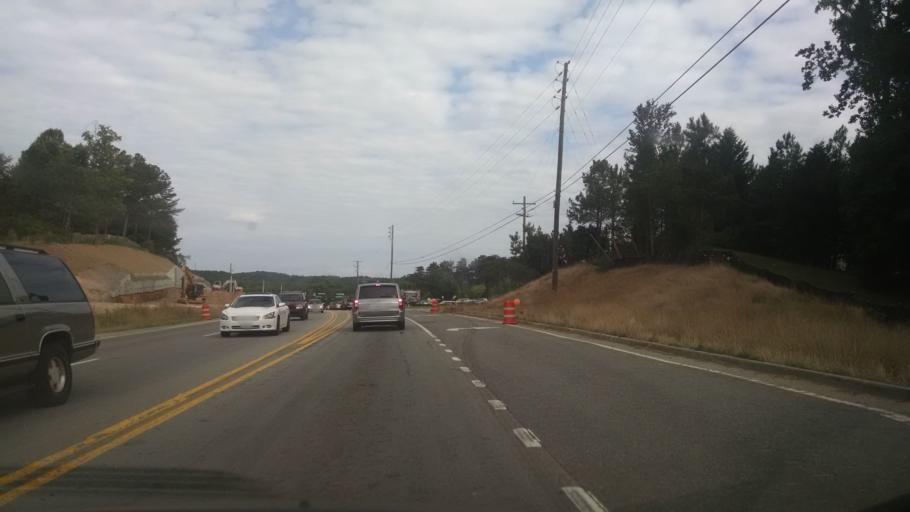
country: US
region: Georgia
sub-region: Gwinnett County
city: Sugar Hill
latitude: 34.1387
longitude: -84.1034
